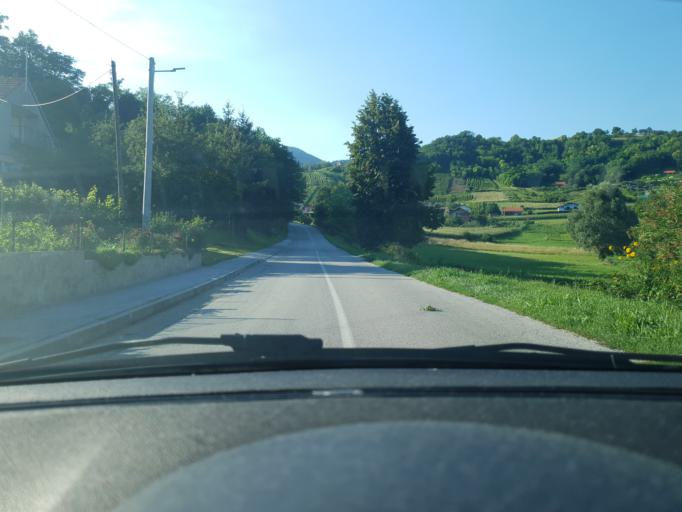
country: HR
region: Krapinsko-Zagorska
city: Radoboj
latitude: 46.1601
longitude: 15.9374
